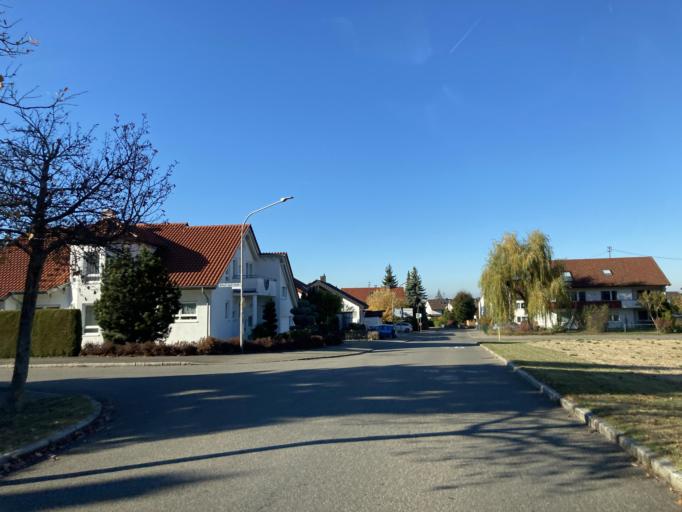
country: DE
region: Baden-Wuerttemberg
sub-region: Tuebingen Region
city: Mossingen
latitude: 48.3997
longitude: 9.0494
